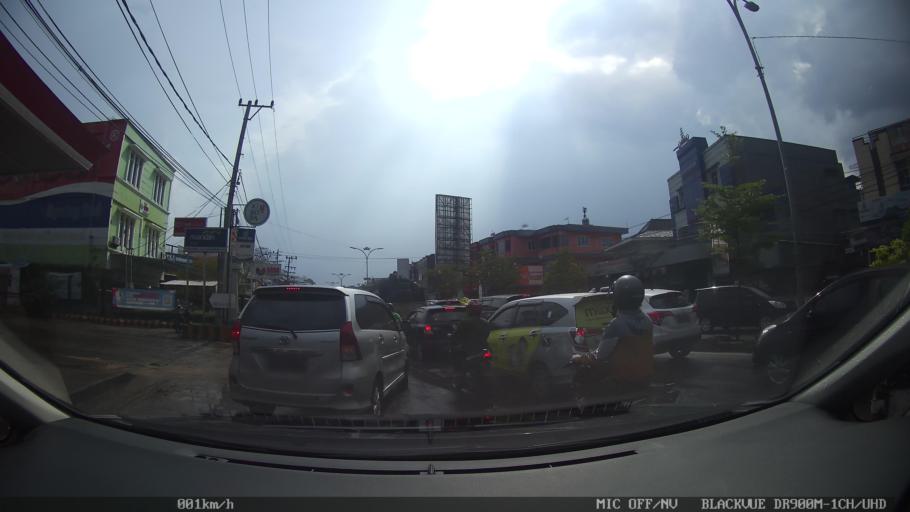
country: ID
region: Lampung
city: Kedaton
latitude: -5.4031
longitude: 105.2817
